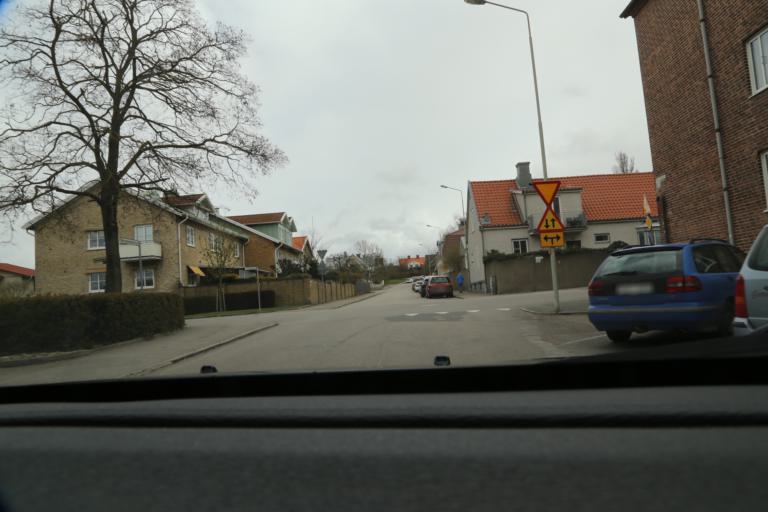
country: SE
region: Halland
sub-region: Varbergs Kommun
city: Varberg
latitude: 57.1065
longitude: 12.2561
